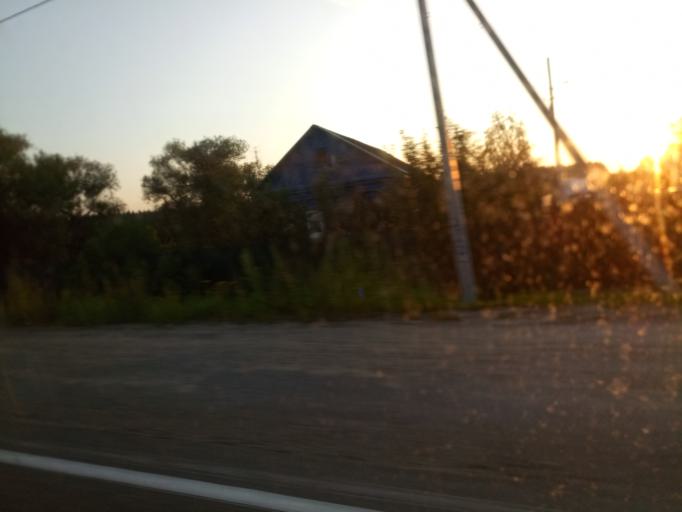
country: RU
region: Moskovskaya
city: Noginsk-9
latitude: 56.0642
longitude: 38.5562
